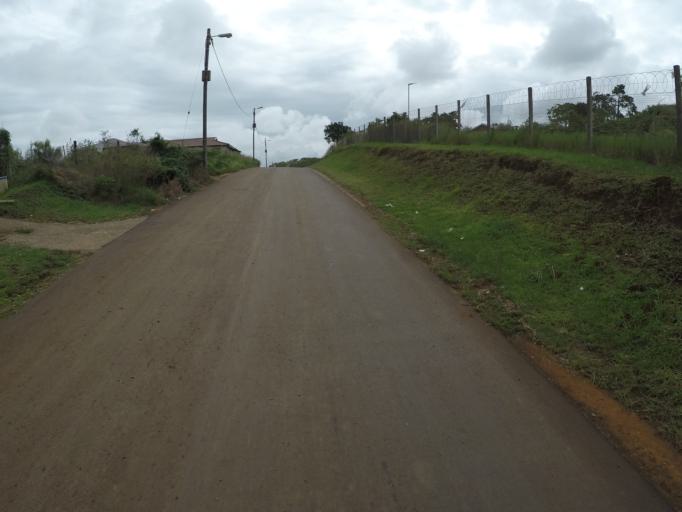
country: ZA
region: KwaZulu-Natal
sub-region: uThungulu District Municipality
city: Empangeni
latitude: -28.7789
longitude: 31.8685
